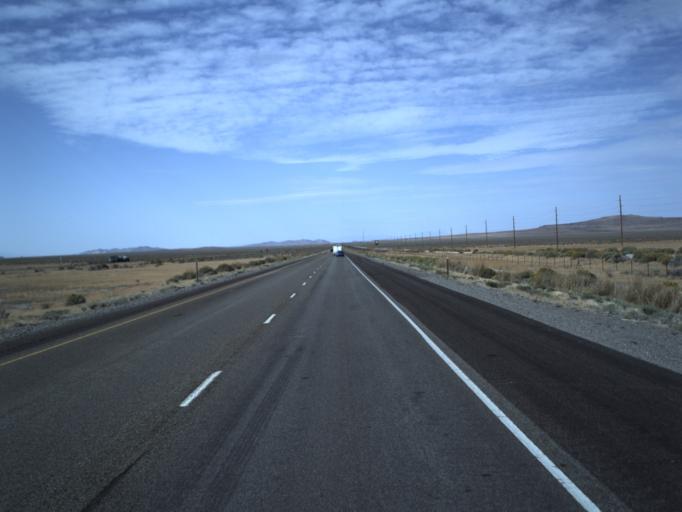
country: US
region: Utah
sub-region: Tooele County
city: Grantsville
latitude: 40.7517
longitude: -113.0439
